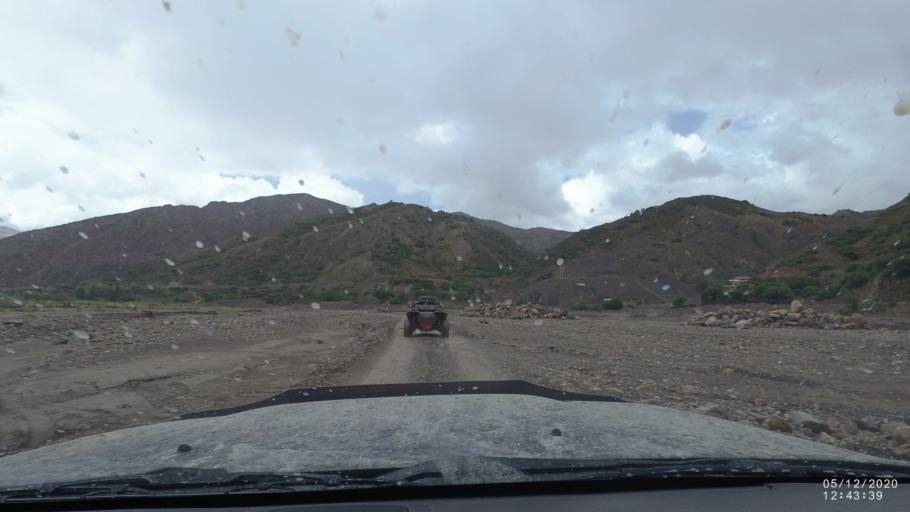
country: BO
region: Cochabamba
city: Sipe Sipe
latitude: -17.5497
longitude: -66.4369
